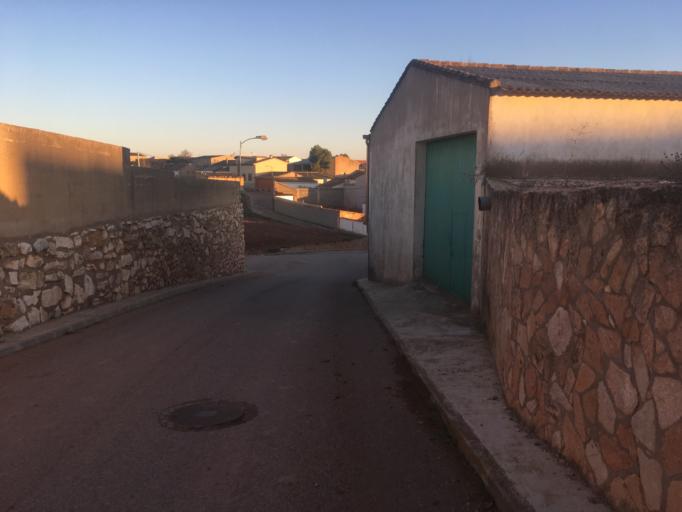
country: ES
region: Castille-La Mancha
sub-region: Provincia de Cuenca
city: Atalaya del Canavate
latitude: 39.5507
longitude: -2.2506
